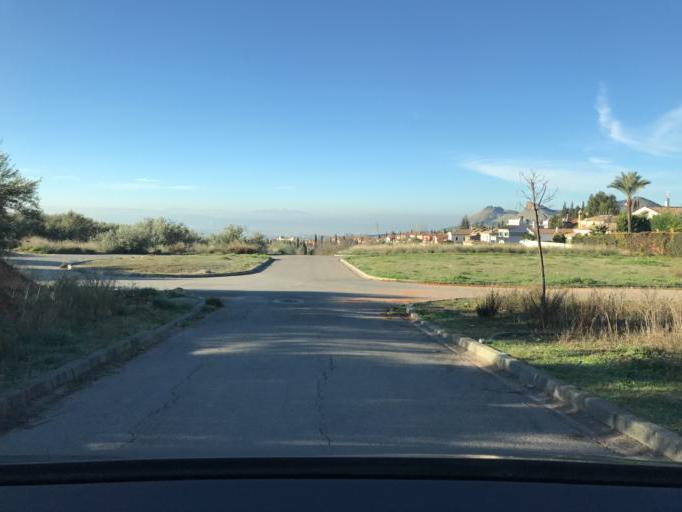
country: ES
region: Andalusia
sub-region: Provincia de Granada
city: Albolote
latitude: 37.2533
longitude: -3.6443
